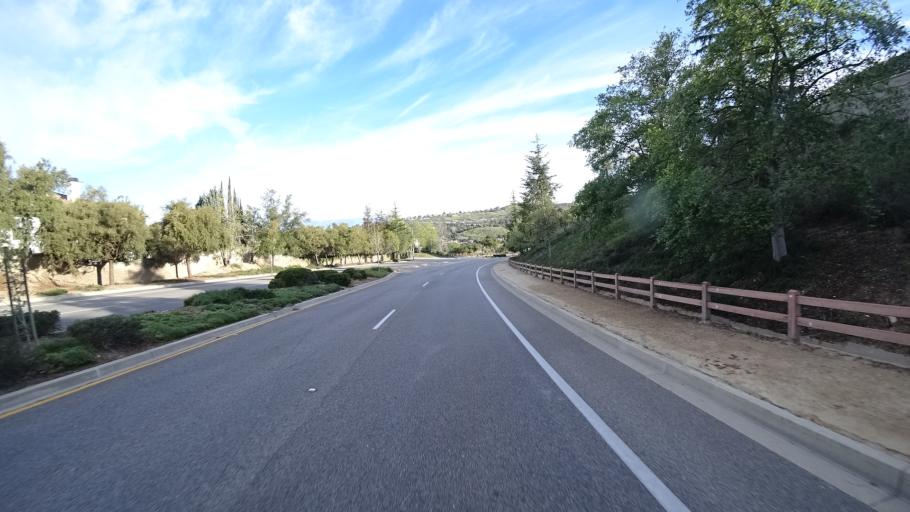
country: US
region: California
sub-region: Ventura County
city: Thousand Oaks
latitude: 34.2055
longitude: -118.8290
